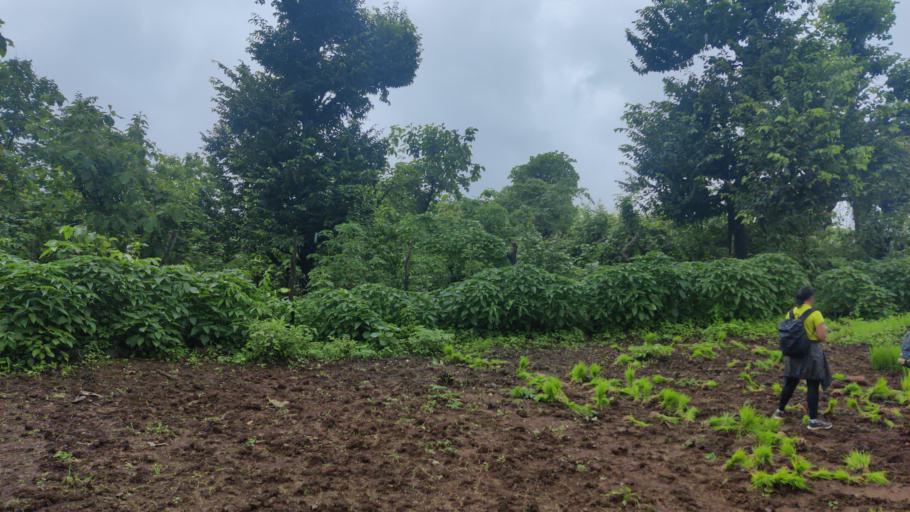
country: IN
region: Maharashtra
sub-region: Thane
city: Thane
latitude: 19.2416
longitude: 72.9572
